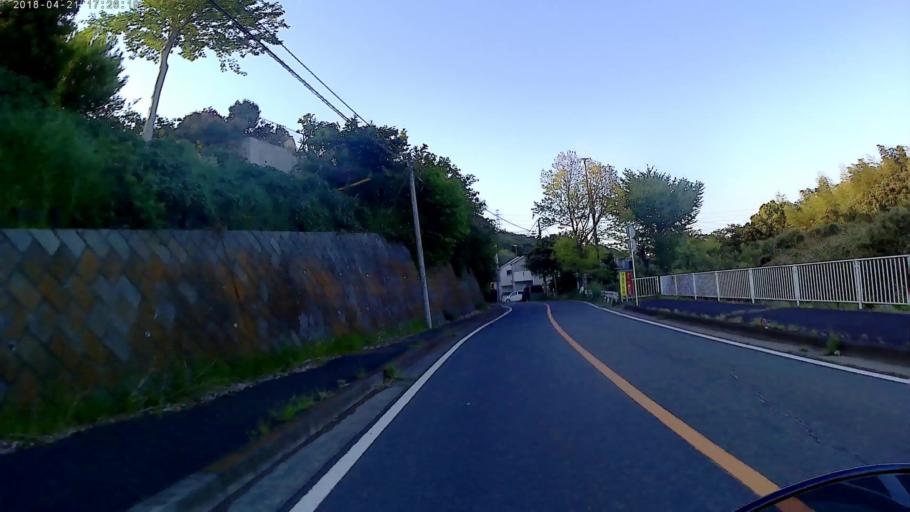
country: JP
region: Kanagawa
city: Atsugi
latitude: 35.4104
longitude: 139.4078
